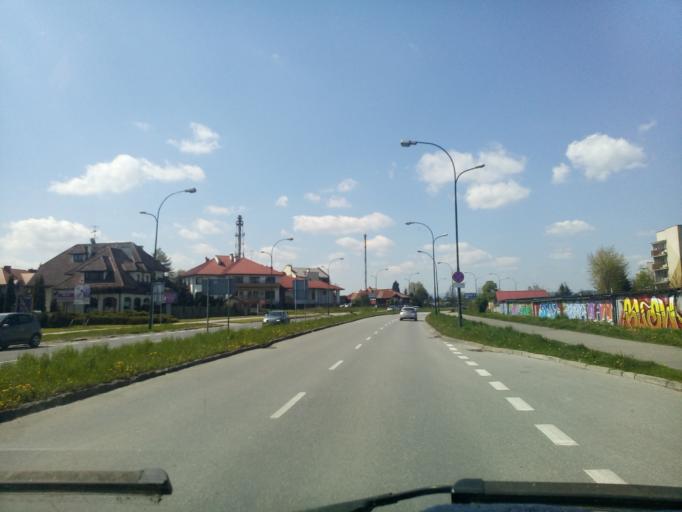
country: PL
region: Lesser Poland Voivodeship
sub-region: Powiat nowosadecki
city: Nowy Sacz
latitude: 49.6086
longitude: 20.7211
